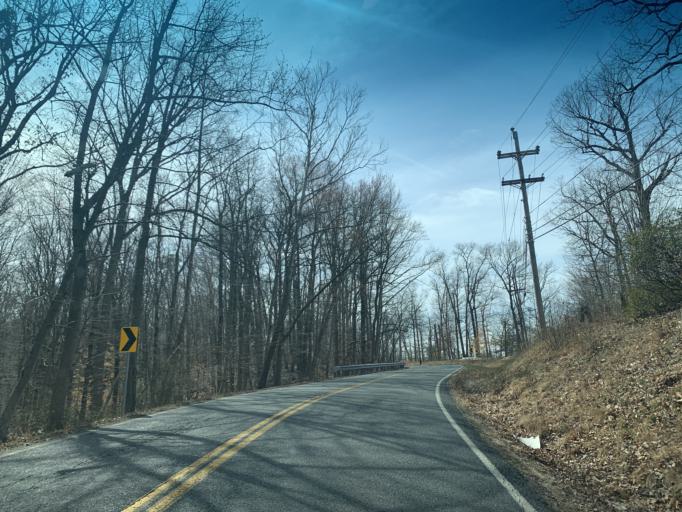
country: US
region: Maryland
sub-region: Cecil County
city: Charlestown
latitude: 39.5691
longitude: -76.0226
